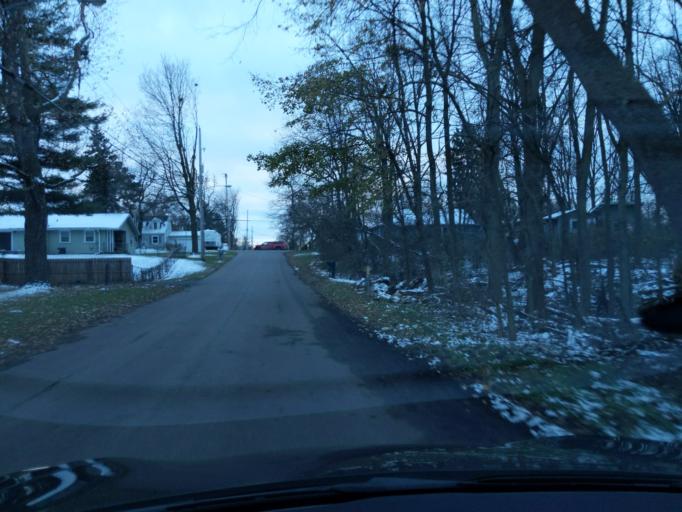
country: US
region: Michigan
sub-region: Ingham County
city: Lansing
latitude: 42.7687
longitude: -84.5496
